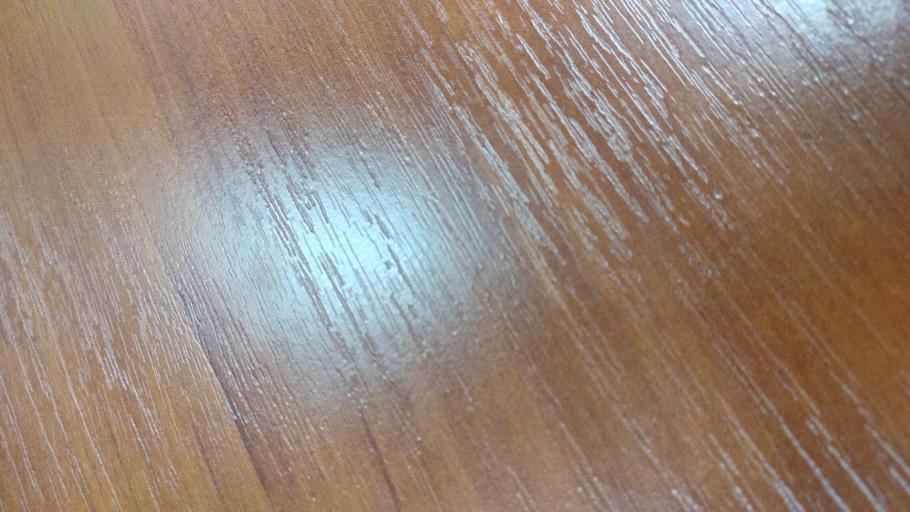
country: RU
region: Tverskaya
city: Zavidovo
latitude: 56.5088
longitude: 36.5109
